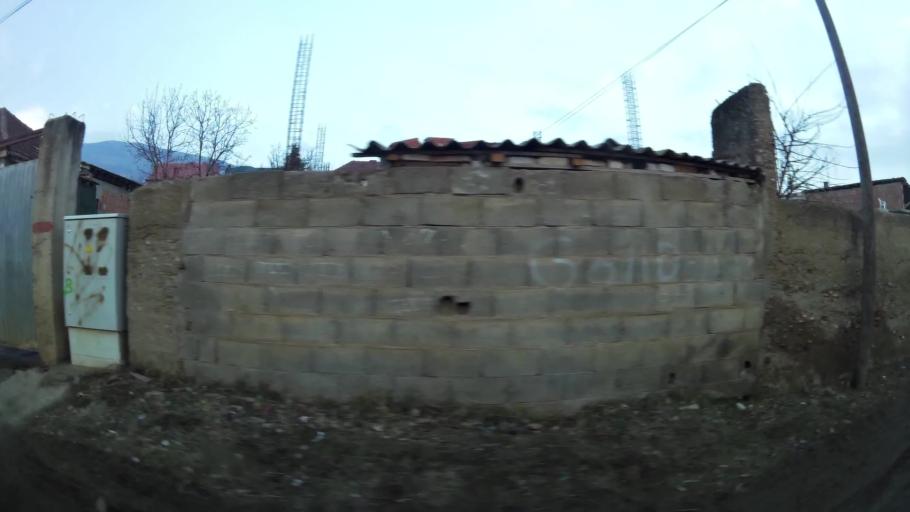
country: MK
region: Aracinovo
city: Arachinovo
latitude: 42.0297
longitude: 21.5593
